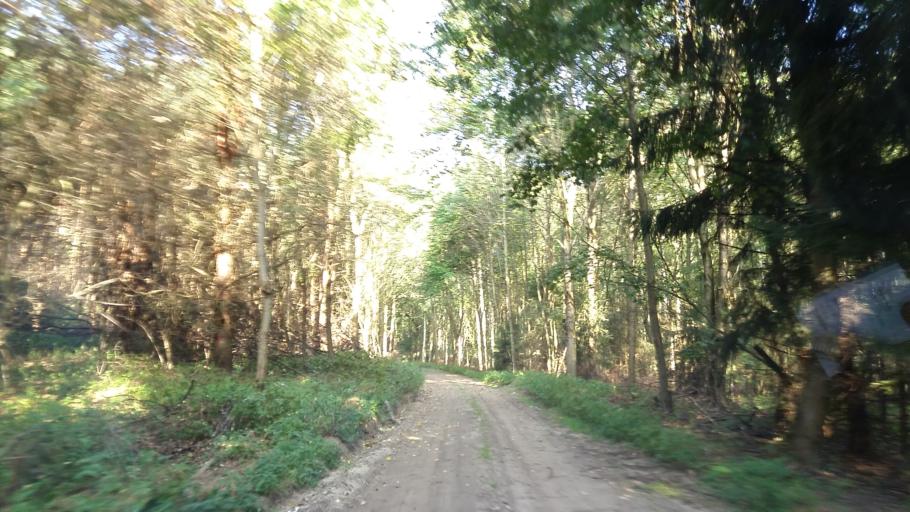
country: PL
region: West Pomeranian Voivodeship
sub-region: Powiat choszczenski
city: Choszczno
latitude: 53.2204
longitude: 15.4551
